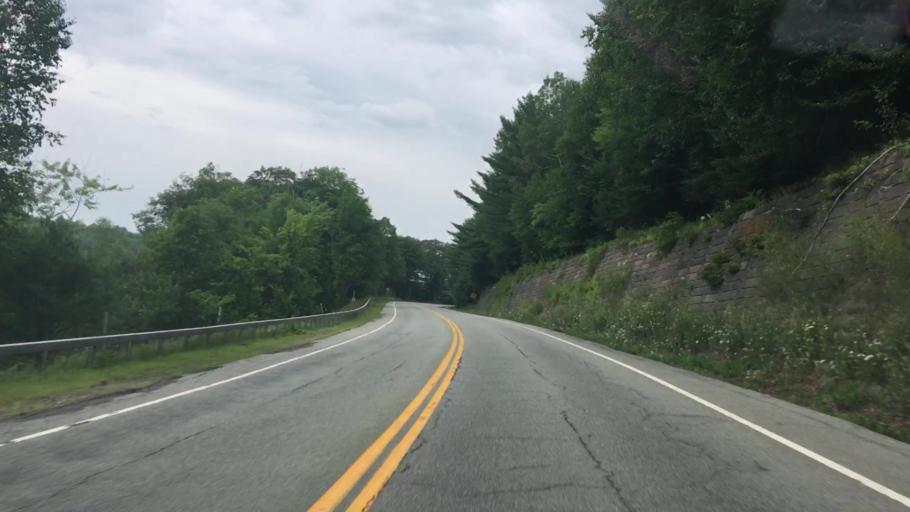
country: US
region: New York
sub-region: Essex County
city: Lake Placid
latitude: 44.2836
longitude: -73.7875
